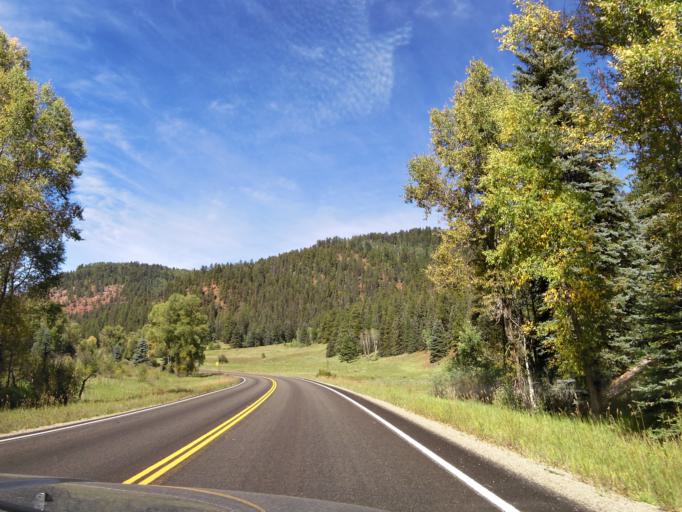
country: US
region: Colorado
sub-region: Montezuma County
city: Mancos
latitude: 37.5934
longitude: -108.1315
